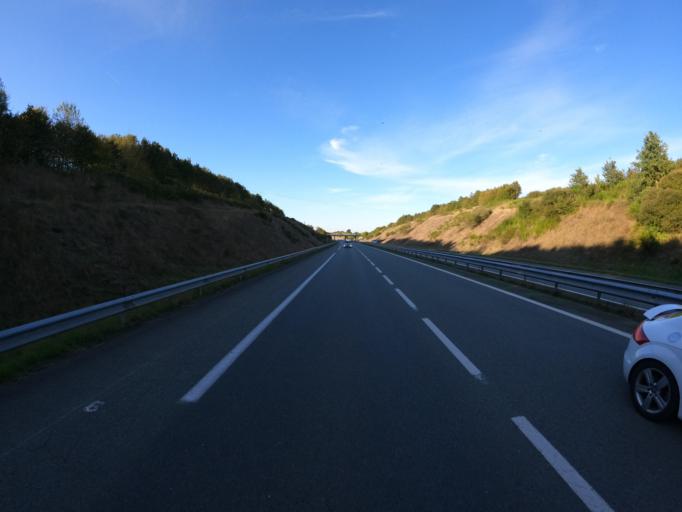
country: FR
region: Pays de la Loire
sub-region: Departement de Maine-et-Loire
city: Nuaille
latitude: 47.0906
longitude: -0.8240
